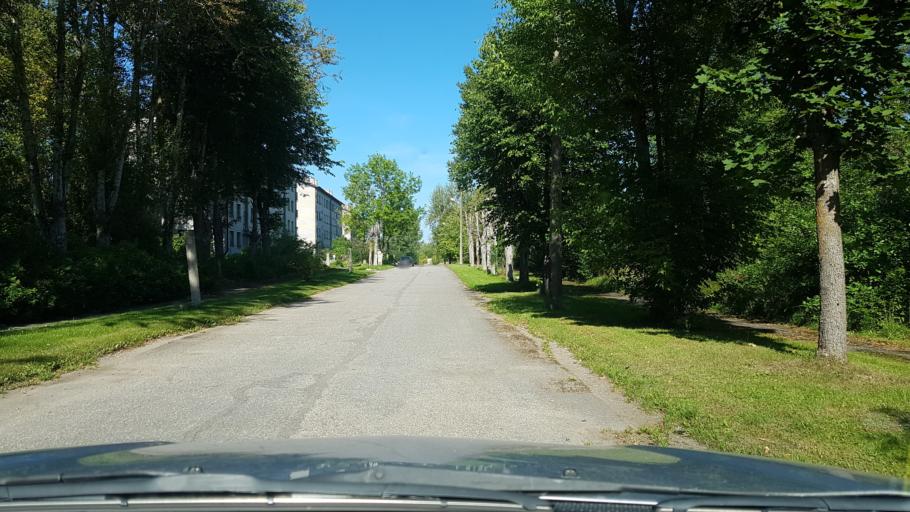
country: EE
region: Ida-Virumaa
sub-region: Sillamaee linn
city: Sillamae
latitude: 59.3212
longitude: 27.7802
